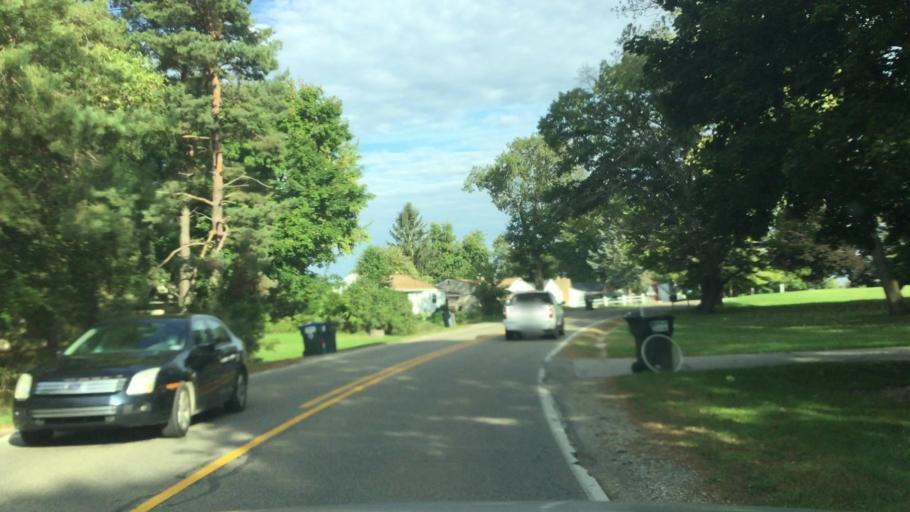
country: US
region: Michigan
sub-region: Livingston County
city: Howell
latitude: 42.5956
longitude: -83.9056
